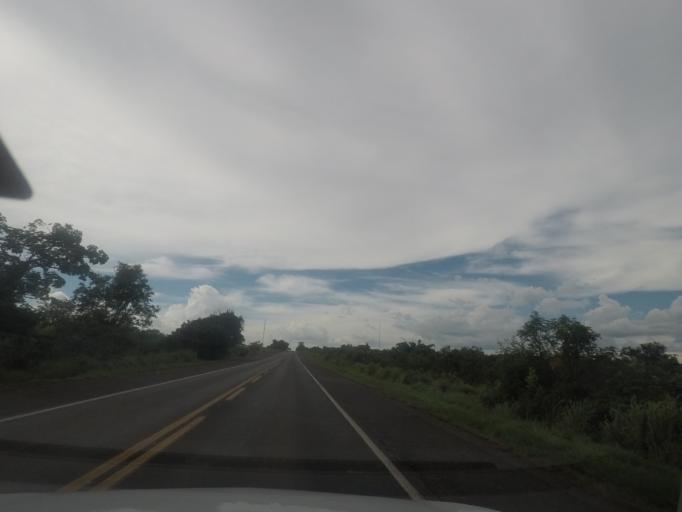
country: BR
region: Minas Gerais
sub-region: Prata
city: Prata
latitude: -19.3175
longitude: -48.9066
